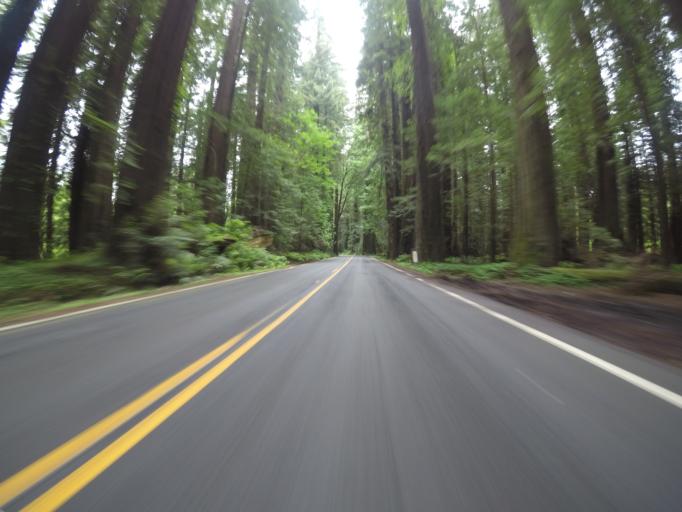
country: US
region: California
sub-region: Humboldt County
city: Rio Dell
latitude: 40.4436
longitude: -124.0212
